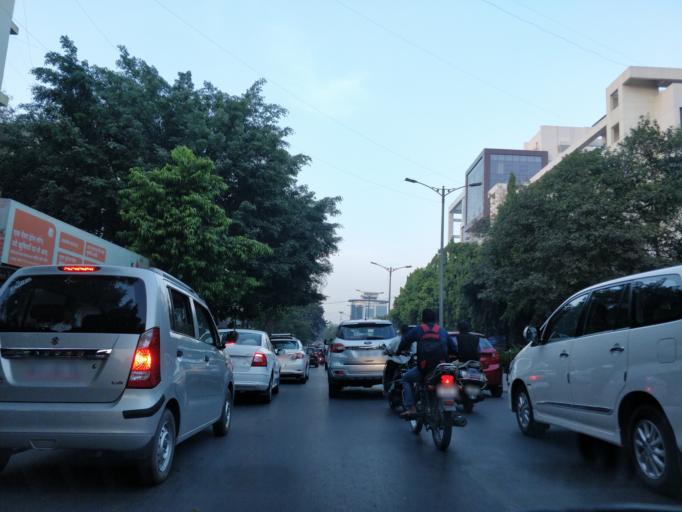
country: IN
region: Maharashtra
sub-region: Pune Division
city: Shivaji Nagar
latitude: 18.5276
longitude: 73.8298
